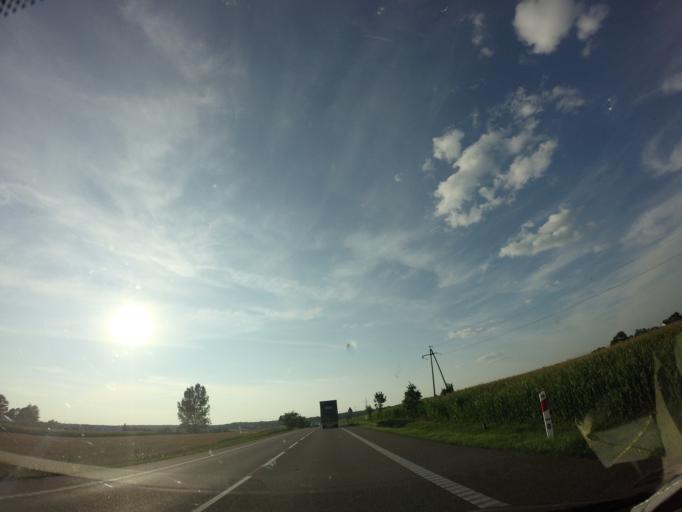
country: PL
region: Podlasie
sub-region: Powiat augustowski
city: Augustow
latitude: 53.7872
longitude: 22.9958
